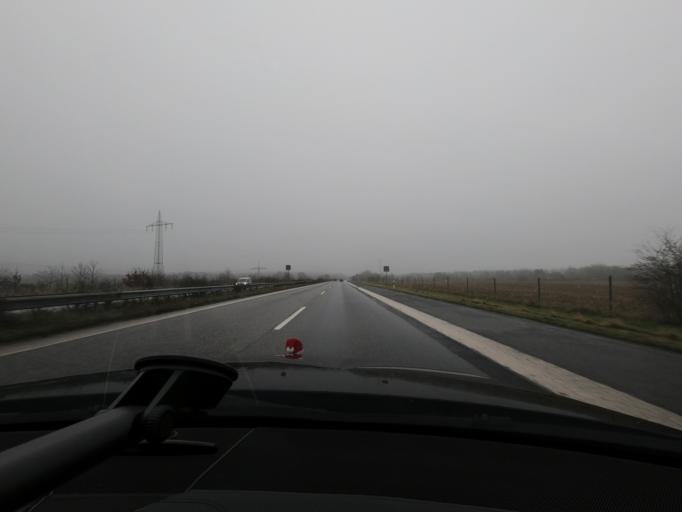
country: DE
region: Schleswig-Holstein
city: Brekendorf
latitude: 54.4068
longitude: 9.6286
